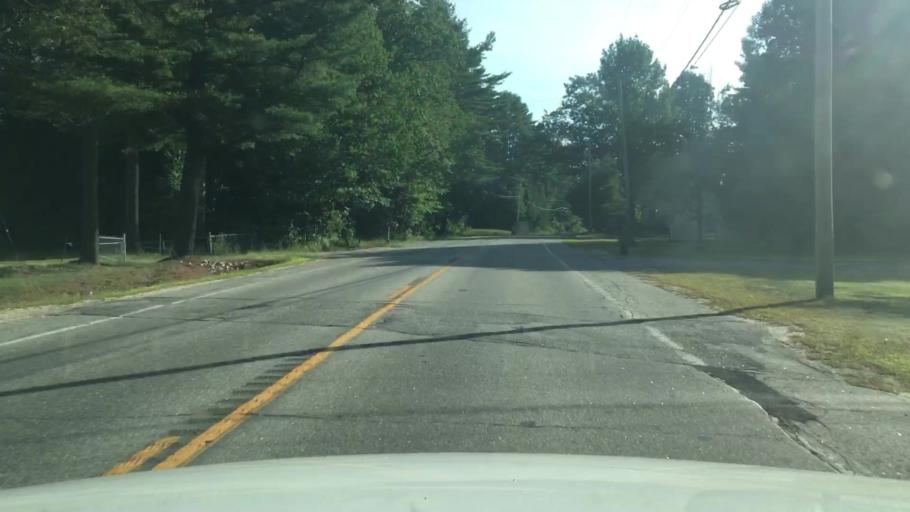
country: US
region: Maine
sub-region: Cumberland County
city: New Gloucester
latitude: 43.9218
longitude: -70.3135
